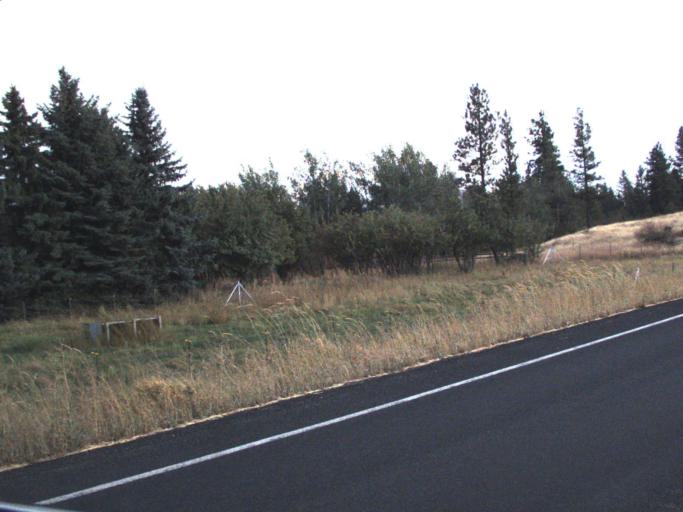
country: US
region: Washington
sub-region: Spokane County
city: Medical Lake
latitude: 47.5453
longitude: -117.7046
